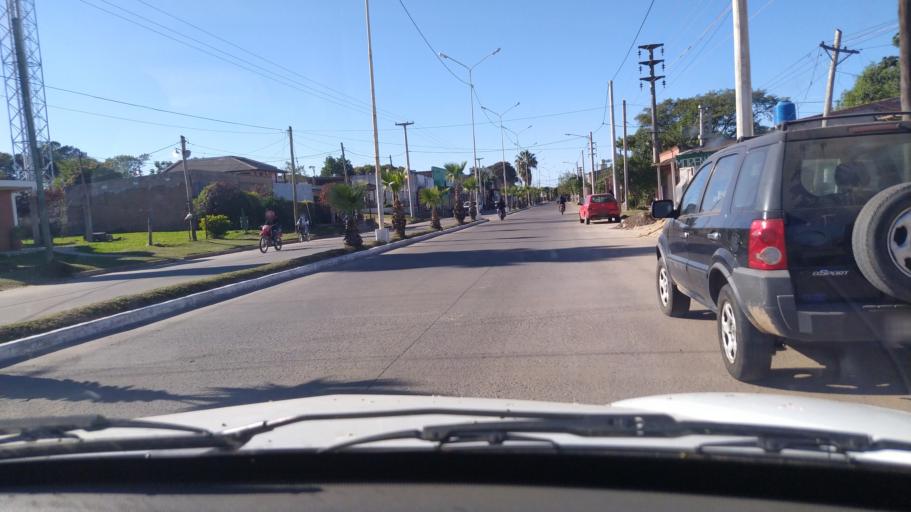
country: AR
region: Corrientes
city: Corrientes
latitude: -27.4949
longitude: -58.8032
